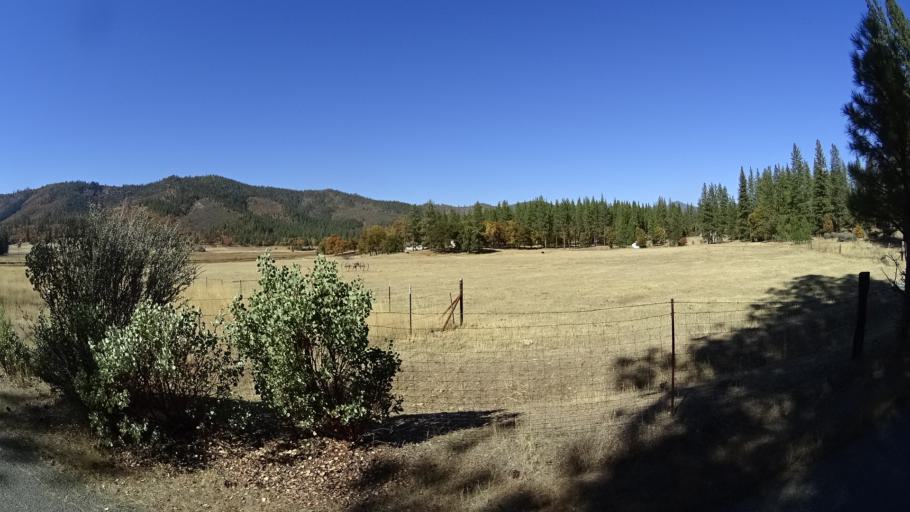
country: US
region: California
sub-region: Siskiyou County
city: Yreka
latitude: 41.5901
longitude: -122.9017
